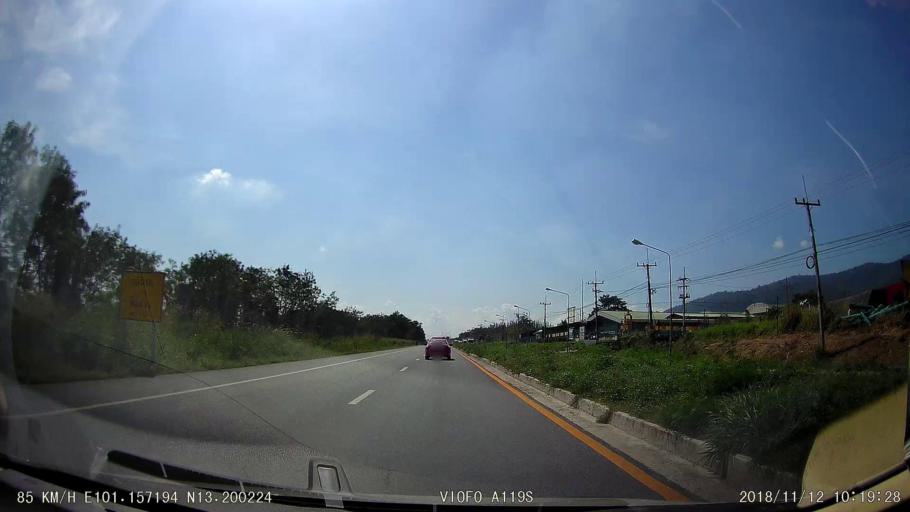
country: TH
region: Chon Buri
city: Ban Bueng
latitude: 13.1997
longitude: 101.1573
